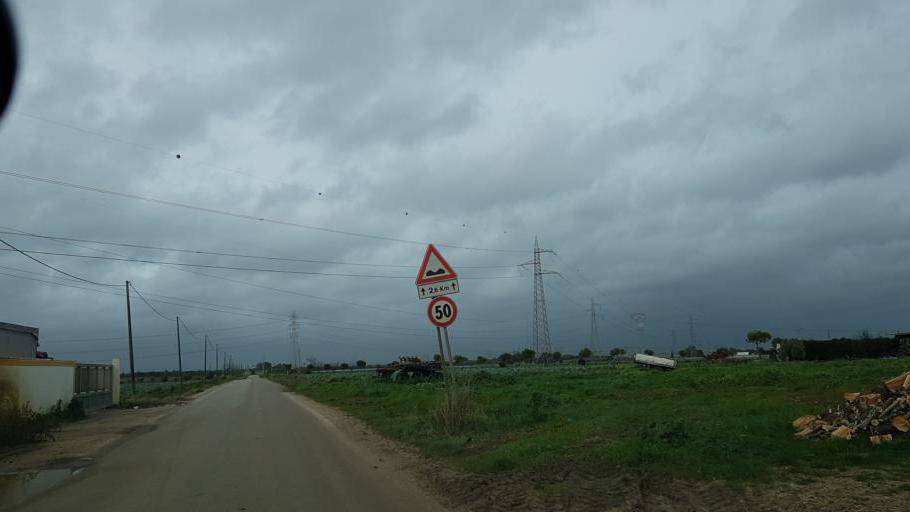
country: IT
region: Apulia
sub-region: Provincia di Brindisi
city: La Rosa
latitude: 40.5932
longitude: 17.9100
